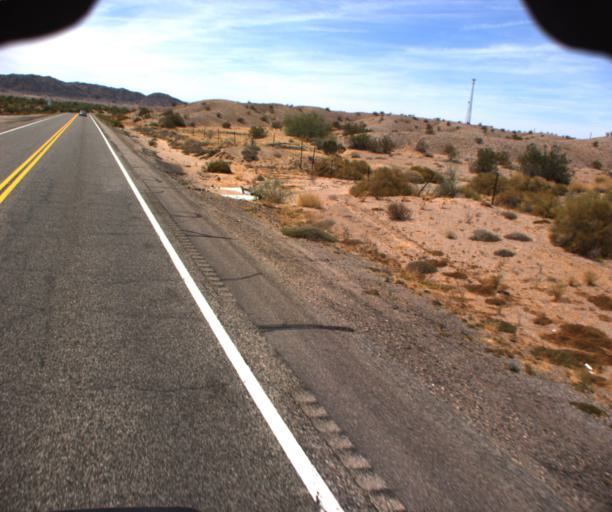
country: US
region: Arizona
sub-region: La Paz County
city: Parker
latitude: 33.9967
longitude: -114.2232
